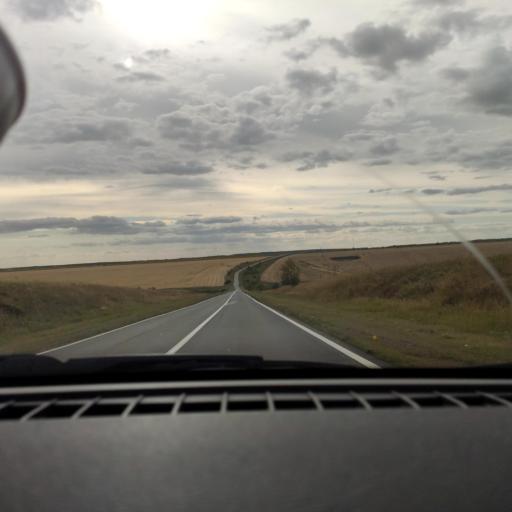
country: RU
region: Samara
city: Georgiyevka
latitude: 53.4166
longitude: 50.8876
